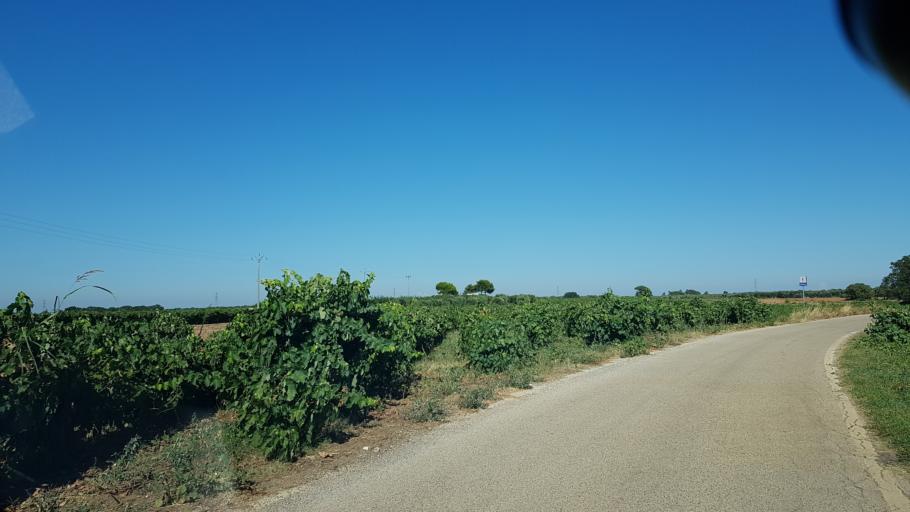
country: IT
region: Apulia
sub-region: Provincia di Brindisi
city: Tuturano
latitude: 40.5679
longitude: 17.8857
